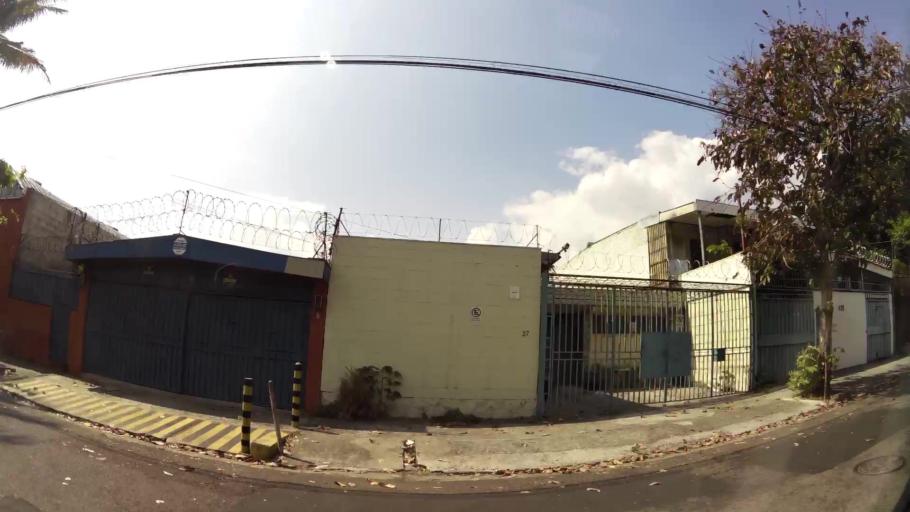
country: SV
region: San Salvador
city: Mejicanos
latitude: 13.7136
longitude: -89.2084
